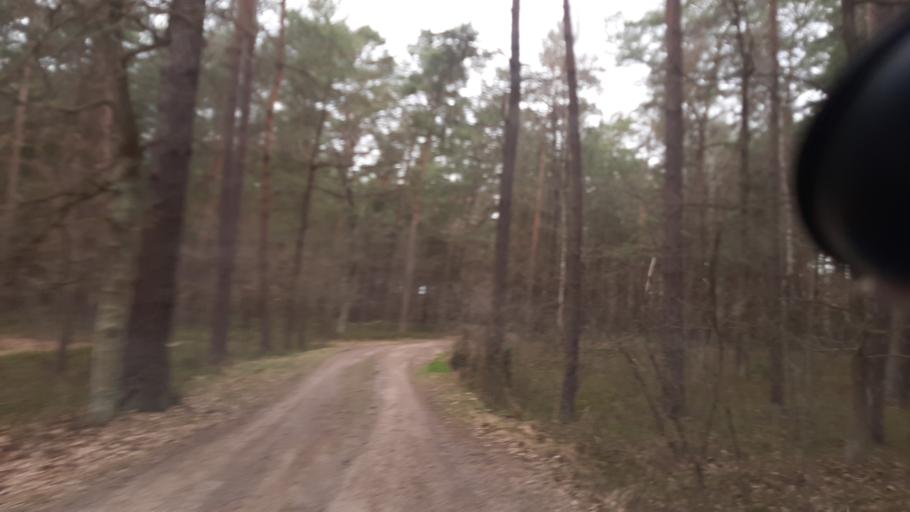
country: PL
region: Lublin Voivodeship
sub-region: Powiat lubartowski
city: Abramow
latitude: 51.4323
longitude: 22.3435
